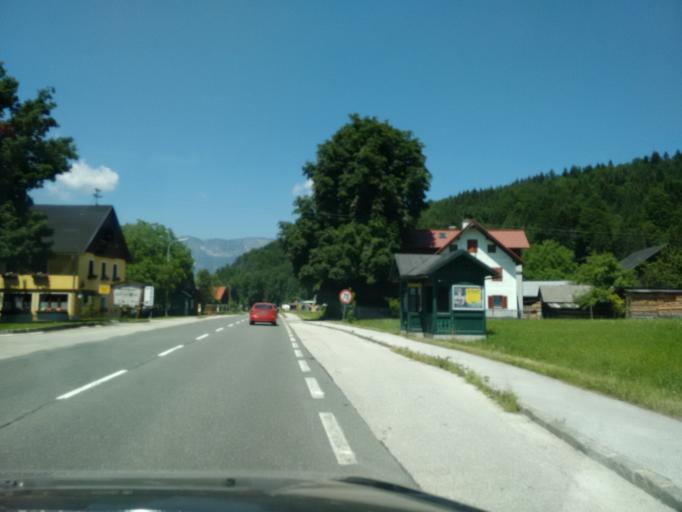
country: AT
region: Upper Austria
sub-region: Politischer Bezirk Gmunden
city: Bad Goisern
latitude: 47.6242
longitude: 13.6449
